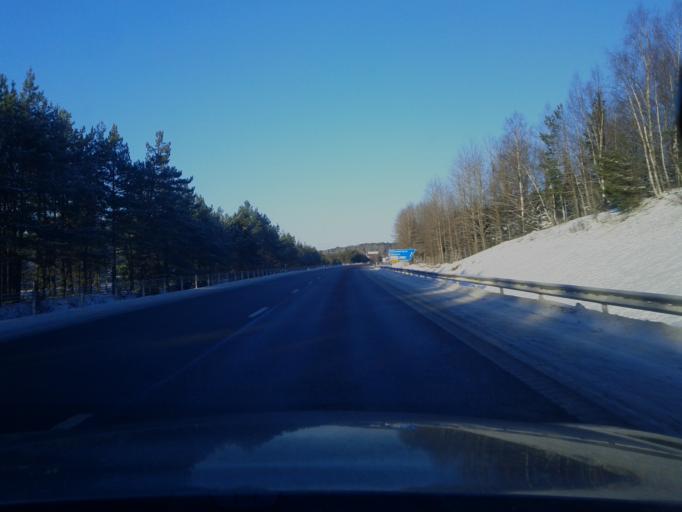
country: SE
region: Uppsala
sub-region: Knivsta Kommun
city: Knivsta
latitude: 59.7360
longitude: 17.8236
